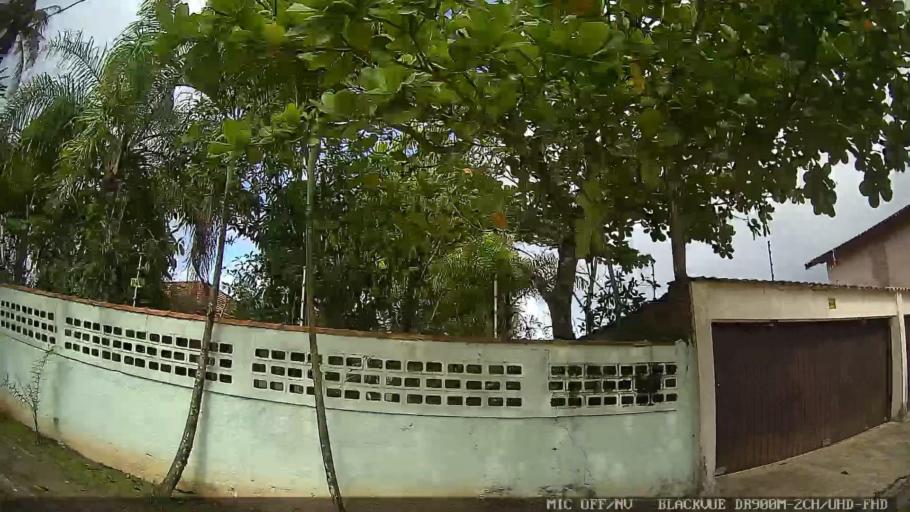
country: BR
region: Sao Paulo
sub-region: Itanhaem
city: Itanhaem
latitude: -24.2360
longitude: -46.8769
